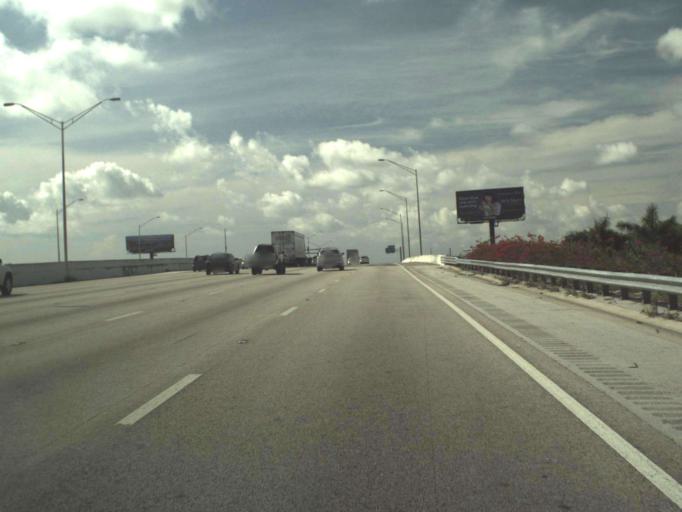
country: US
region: Florida
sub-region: Palm Beach County
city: Mangonia Park
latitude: 26.7737
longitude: -80.0972
